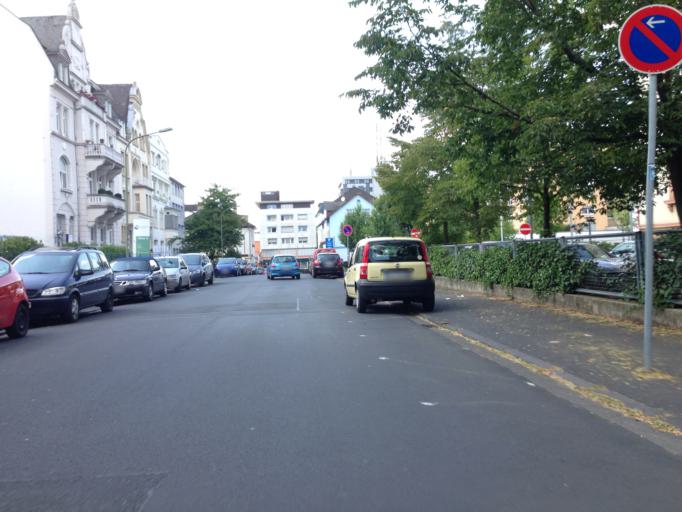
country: DE
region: Hesse
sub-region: Regierungsbezirk Giessen
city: Giessen
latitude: 50.5786
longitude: 8.6685
